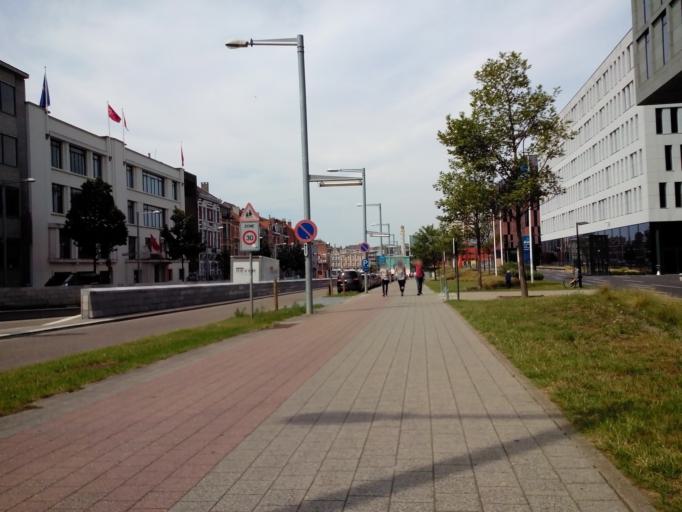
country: BE
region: Flanders
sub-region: Provincie Vlaams-Brabant
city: Leuven
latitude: 50.8786
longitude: 4.7160
